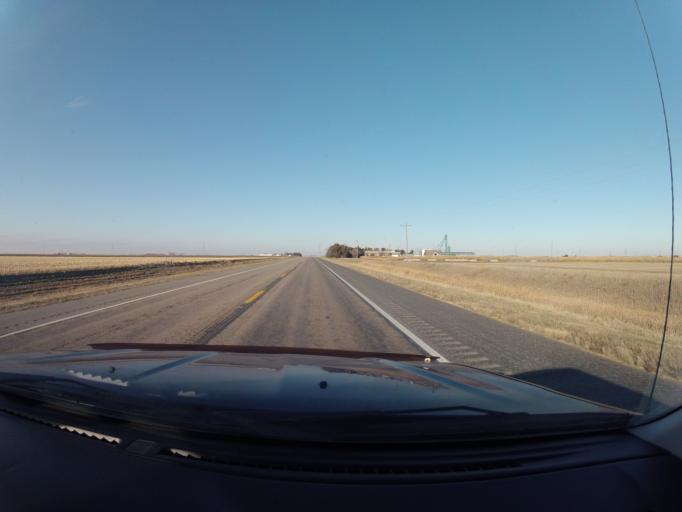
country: US
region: Nebraska
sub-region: Kearney County
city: Minden
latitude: 40.5349
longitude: -98.9518
